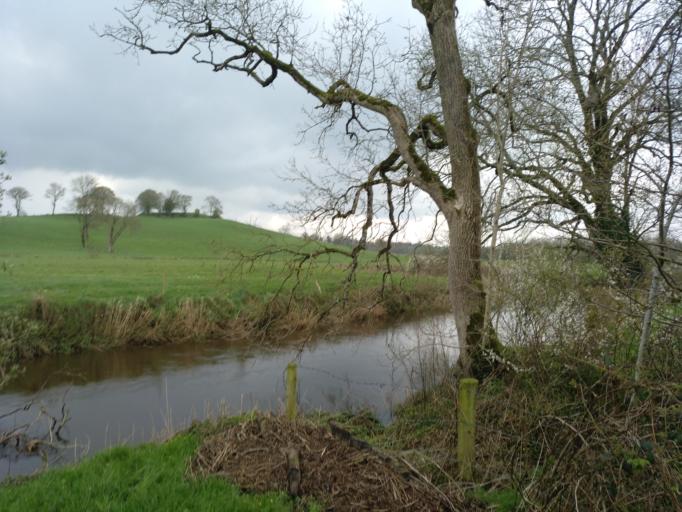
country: IE
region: Ulster
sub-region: County Monaghan
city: Clones
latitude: 54.1901
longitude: -7.1547
